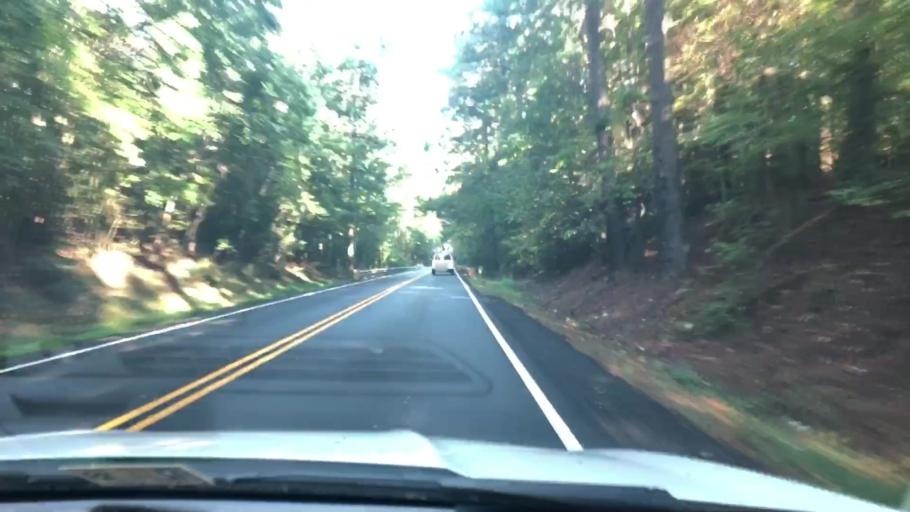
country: US
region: Virginia
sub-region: King William County
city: West Point
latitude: 37.4824
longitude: -76.8516
